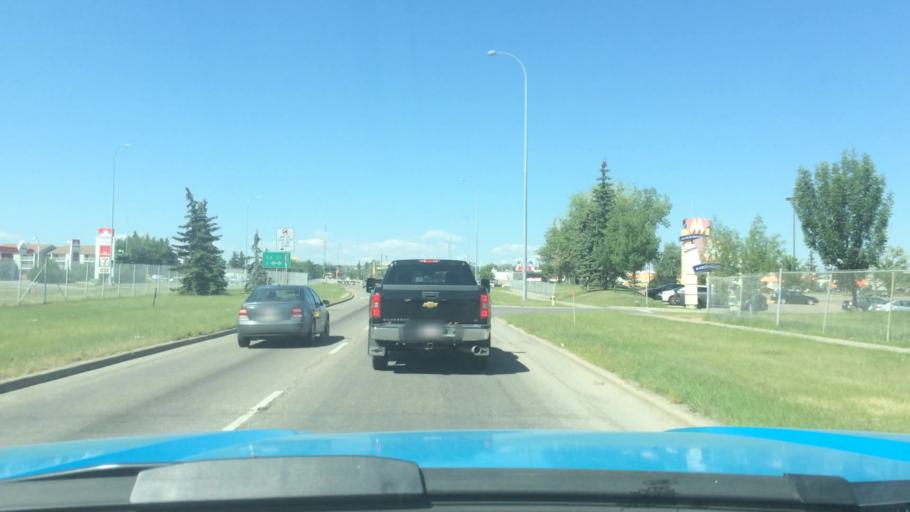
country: CA
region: Alberta
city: Calgary
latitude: 51.0526
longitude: -113.9786
